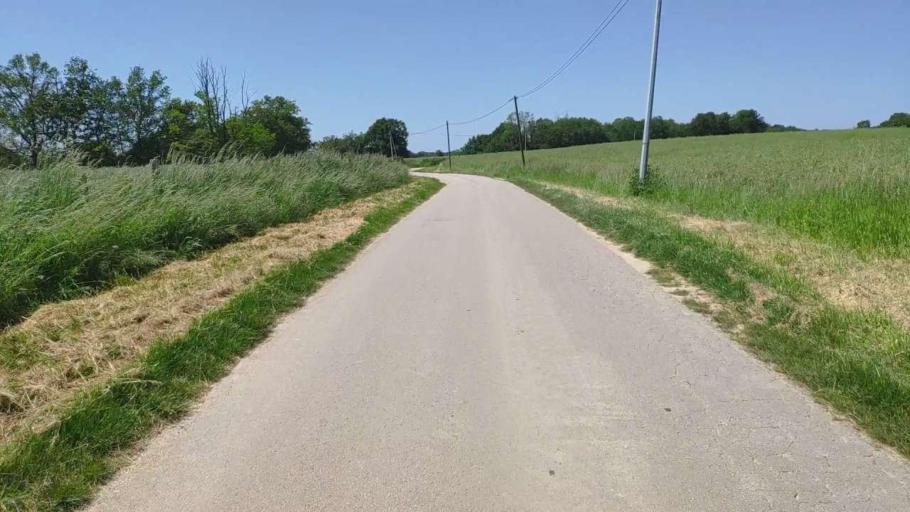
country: FR
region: Franche-Comte
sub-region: Departement du Jura
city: Bletterans
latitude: 46.7709
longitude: 5.4067
